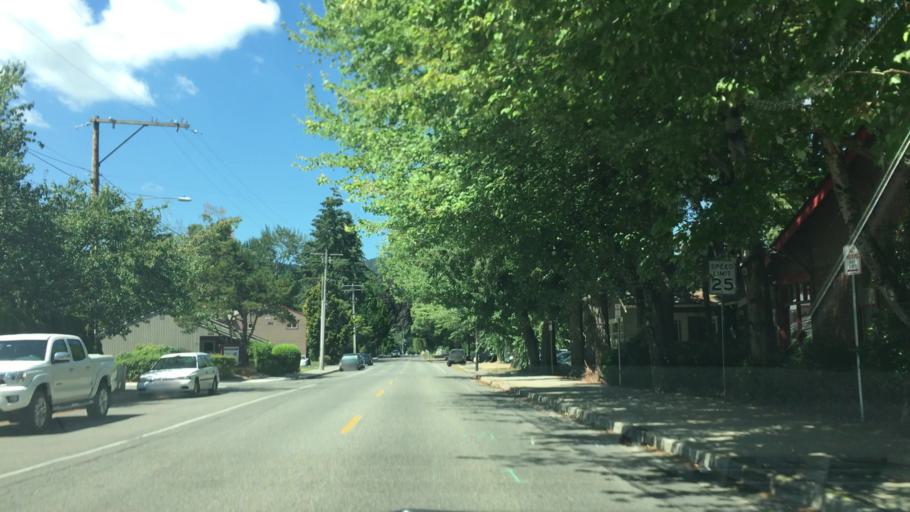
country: US
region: Washington
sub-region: King County
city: Issaquah
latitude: 47.5395
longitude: -122.0398
